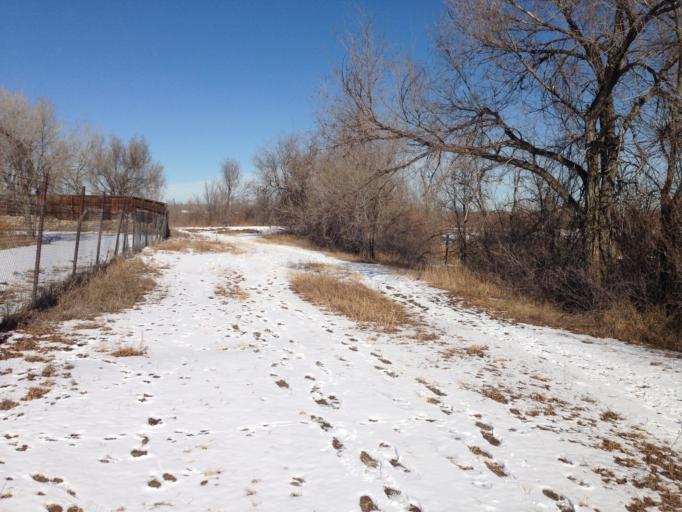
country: US
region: Colorado
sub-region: Adams County
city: Berkley
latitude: 39.7956
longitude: -105.0386
